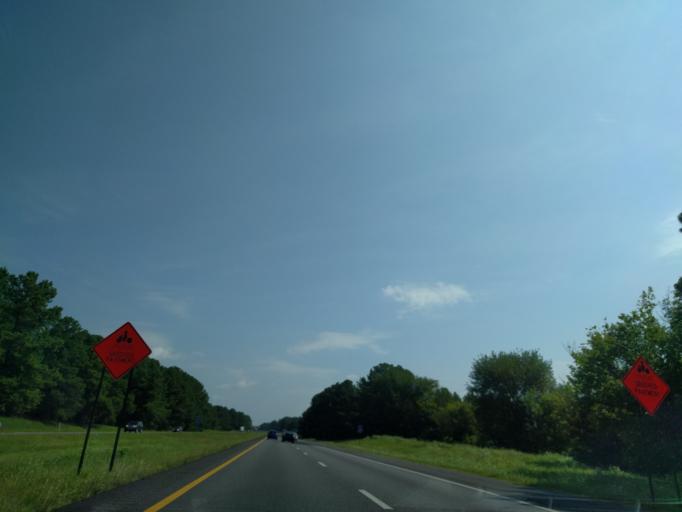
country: US
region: Tennessee
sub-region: Sumner County
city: Portland
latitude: 36.5960
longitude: -86.5937
